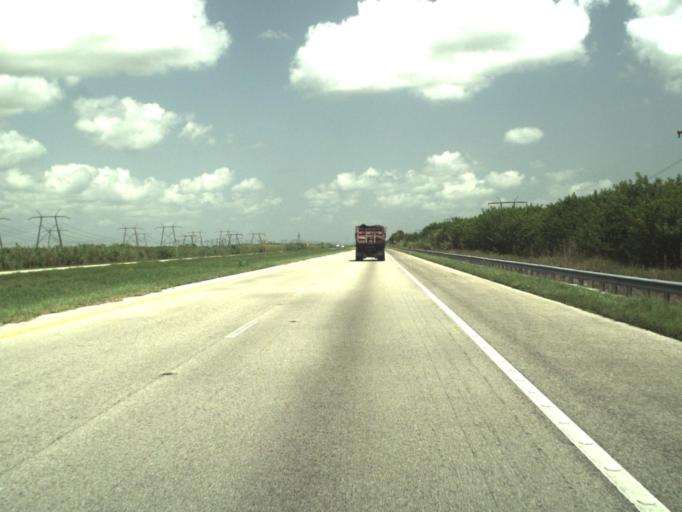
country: US
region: Florida
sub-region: Broward County
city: Weston
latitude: 26.2833
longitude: -80.4979
